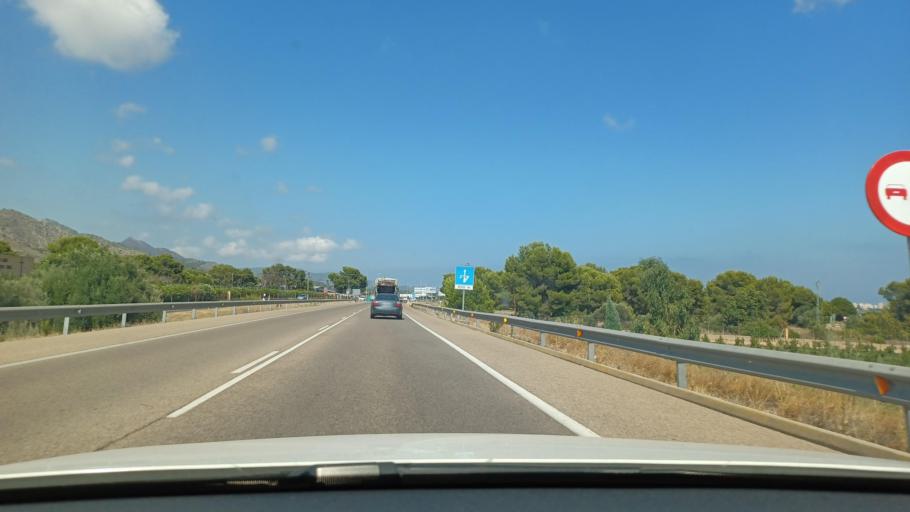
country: ES
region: Valencia
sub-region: Provincia de Castello
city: Castello de la Plana
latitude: 40.0262
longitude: -0.0055
